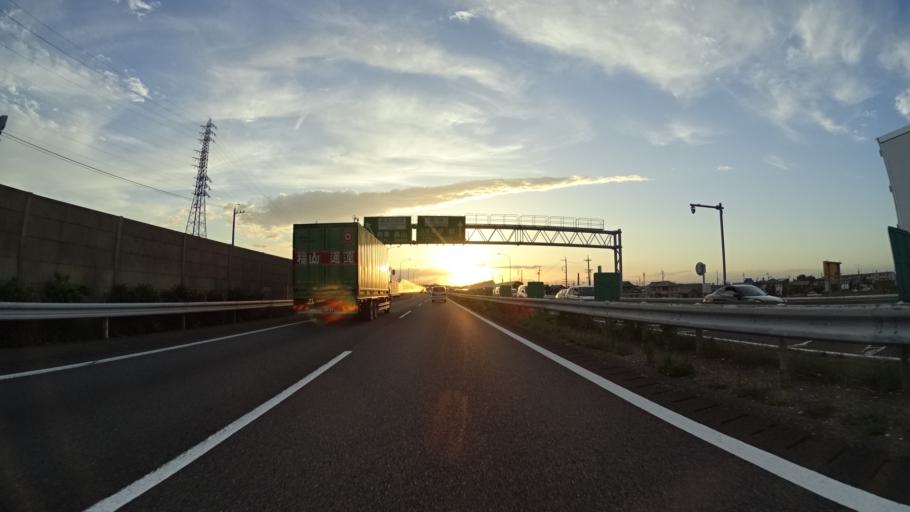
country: JP
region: Aichi
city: Ichinomiya
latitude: 35.2801
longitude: 136.7955
